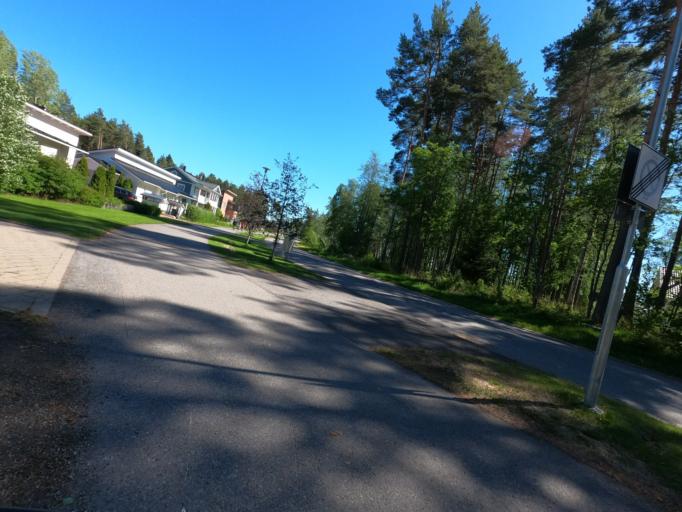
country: FI
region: North Karelia
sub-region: Joensuu
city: Joensuu
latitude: 62.5780
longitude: 29.7655
